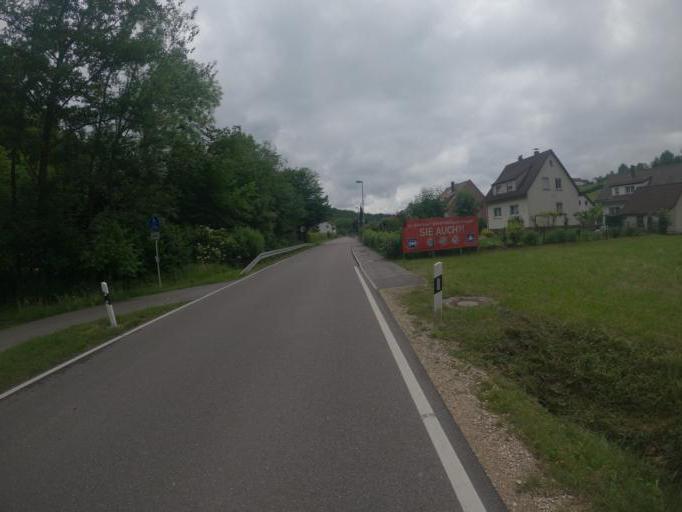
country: DE
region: Baden-Wuerttemberg
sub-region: Regierungsbezirk Stuttgart
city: Ebersbach an der Fils
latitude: 48.7285
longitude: 9.5575
